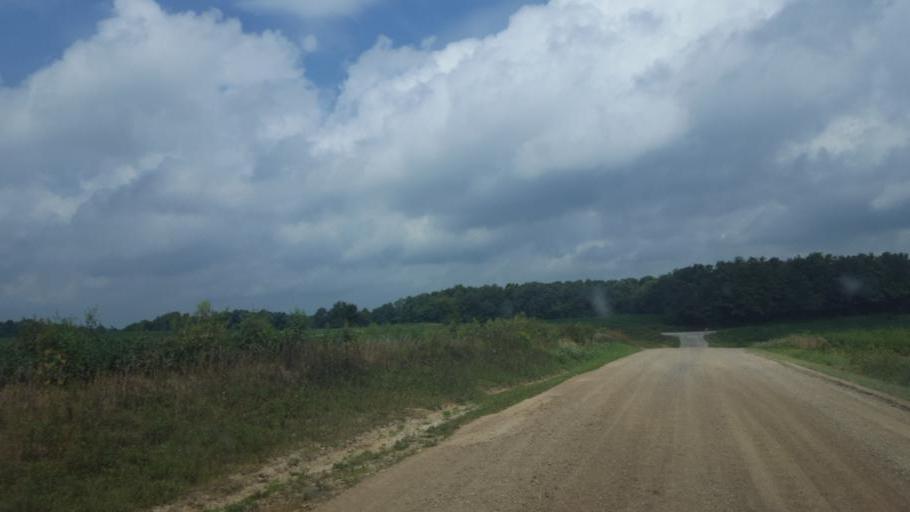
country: US
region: Ohio
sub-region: Morrow County
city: Mount Gilead
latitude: 40.5612
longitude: -82.7150
